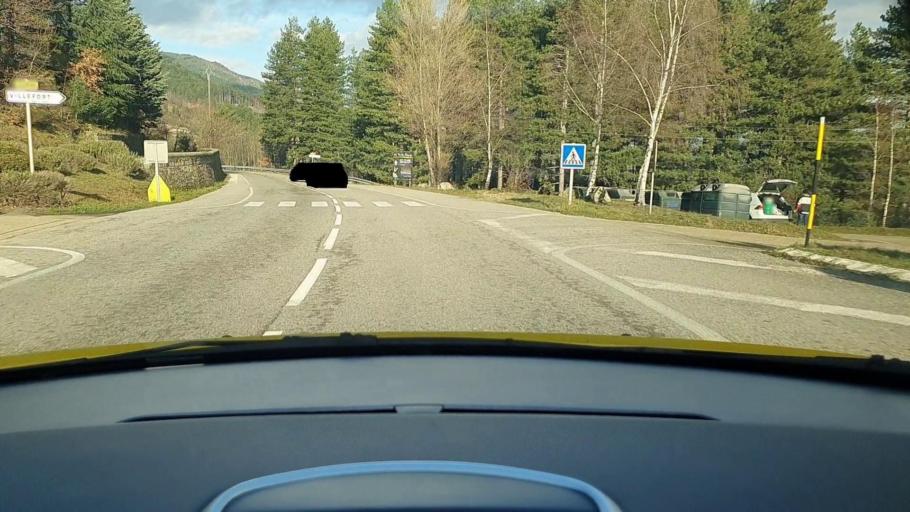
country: FR
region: Languedoc-Roussillon
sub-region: Departement du Gard
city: Branoux-les-Taillades
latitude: 44.3782
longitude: 3.9422
